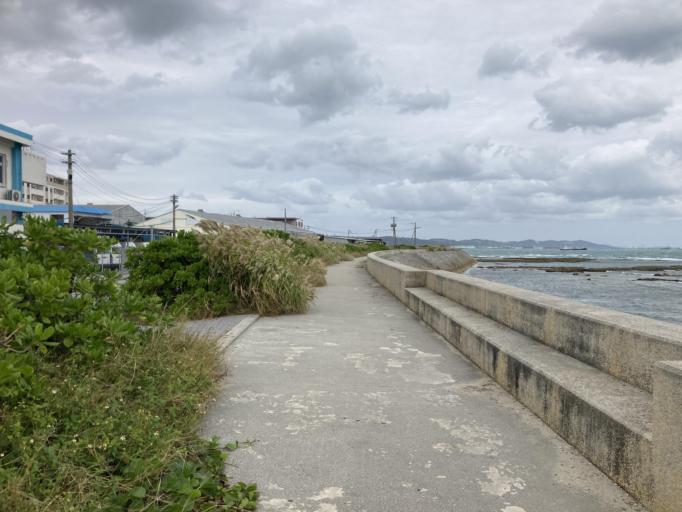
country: JP
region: Okinawa
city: Ginowan
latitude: 26.1848
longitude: 127.7783
